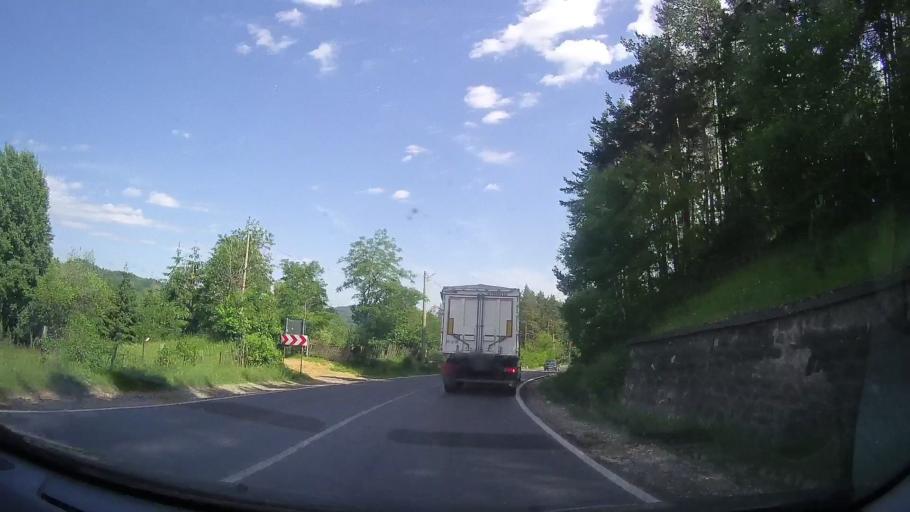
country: RO
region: Prahova
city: Maneciu
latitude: 45.3276
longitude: 25.9799
